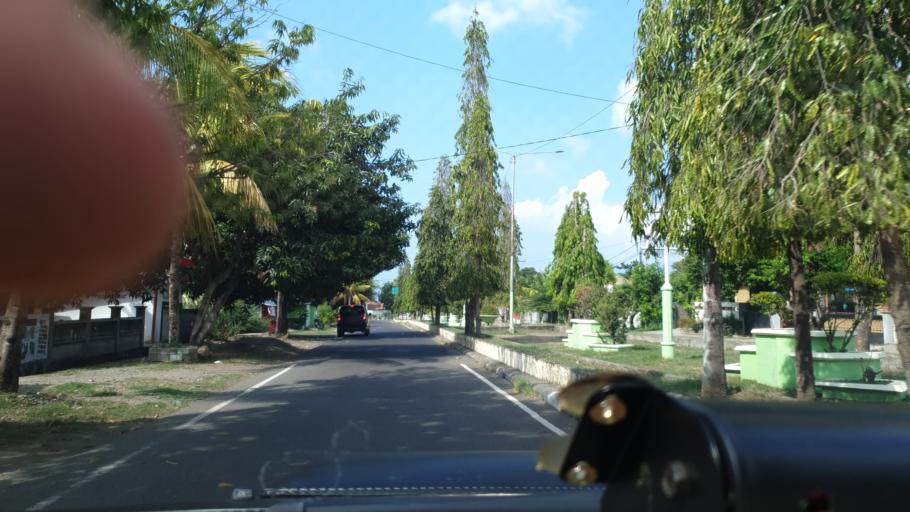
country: ID
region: East Nusa Tenggara
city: Waioti
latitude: -8.6304
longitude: 122.2367
